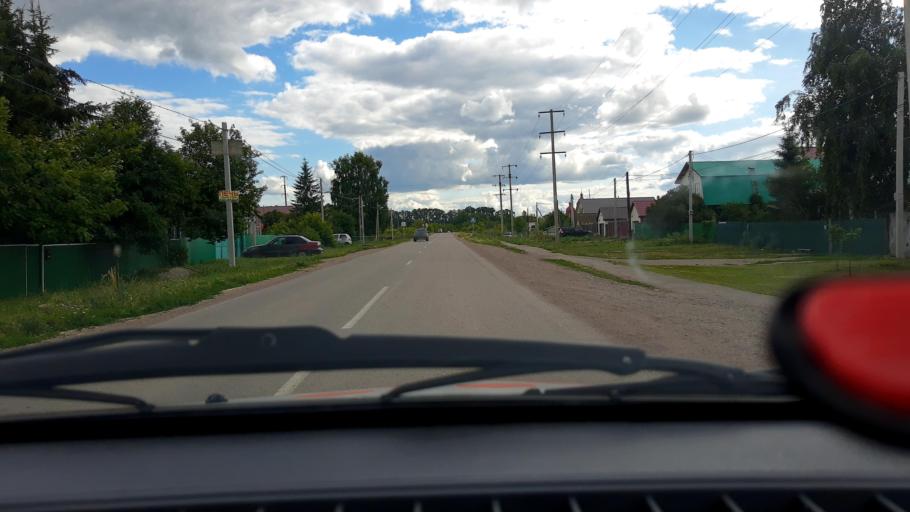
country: RU
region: Bashkortostan
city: Kabakovo
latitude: 54.5163
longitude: 55.9452
